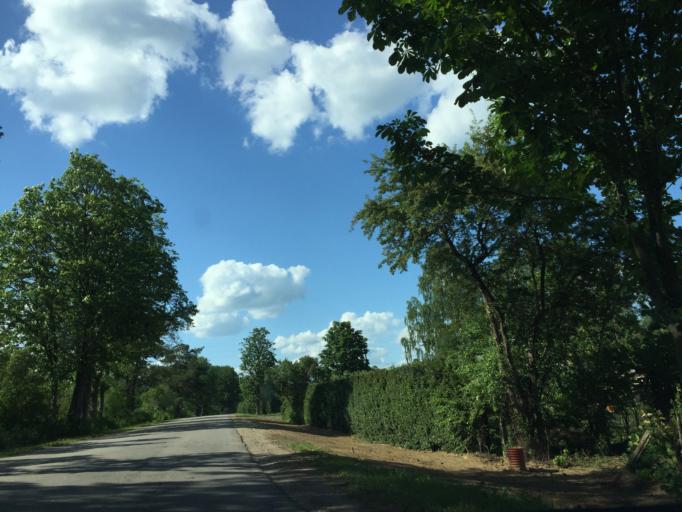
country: LV
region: Jaunpils
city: Jaunpils
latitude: 56.8766
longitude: 22.9924
